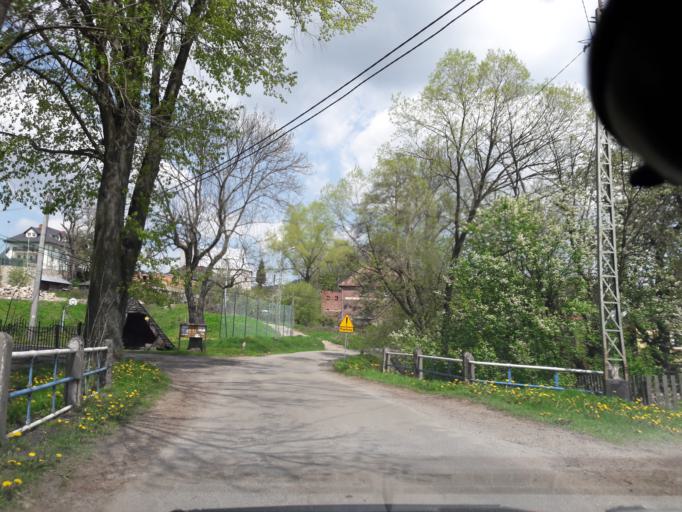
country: PL
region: Lower Silesian Voivodeship
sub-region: Powiat klodzki
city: Duszniki-Zdroj
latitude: 50.4331
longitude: 16.3589
